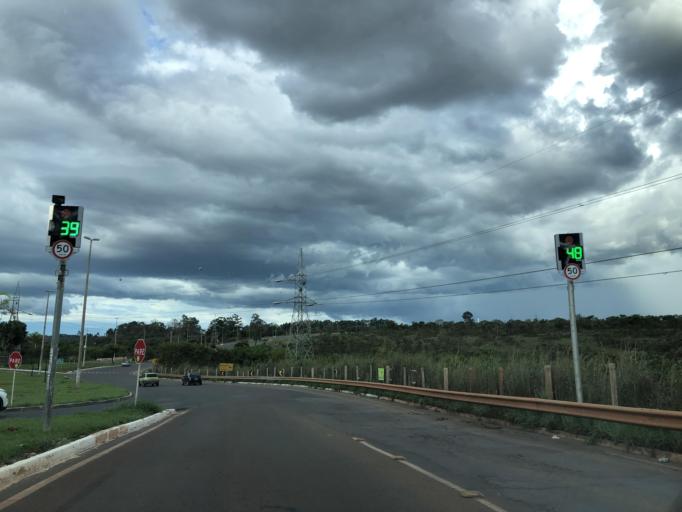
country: BR
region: Goias
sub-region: Luziania
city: Luziania
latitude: -16.0392
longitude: -48.0556
